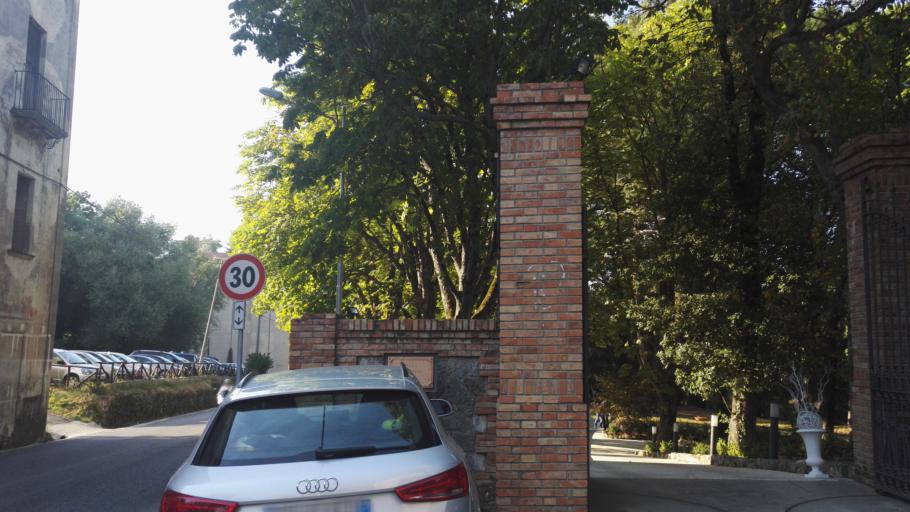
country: IT
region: Calabria
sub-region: Provincia di Cosenza
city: Carolei
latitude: 39.2489
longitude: 16.2181
